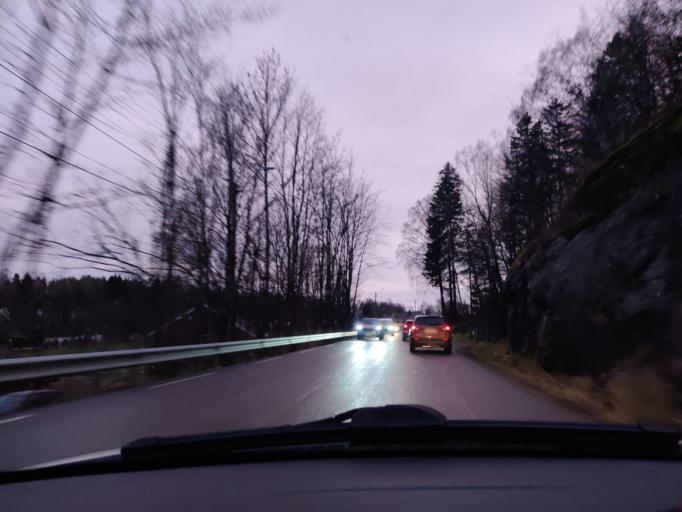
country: NO
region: Vestfold
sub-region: Tonsberg
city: Sem
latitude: 59.2712
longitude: 10.3662
